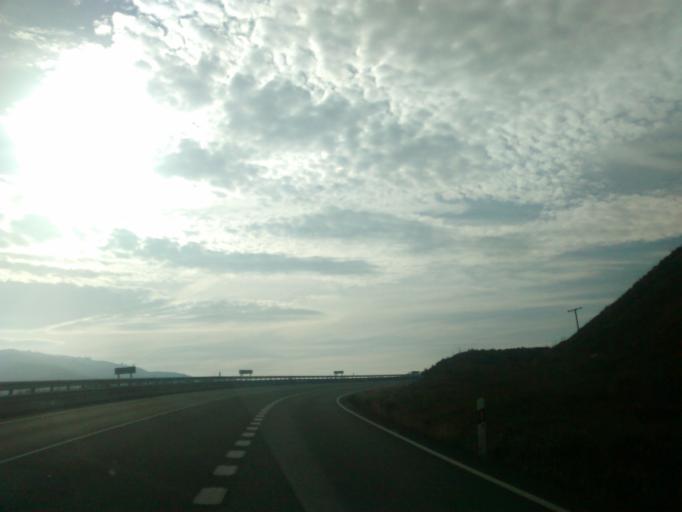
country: ES
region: La Rioja
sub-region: Provincia de La Rioja
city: Cenicero
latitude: 42.4673
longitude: -2.6173
